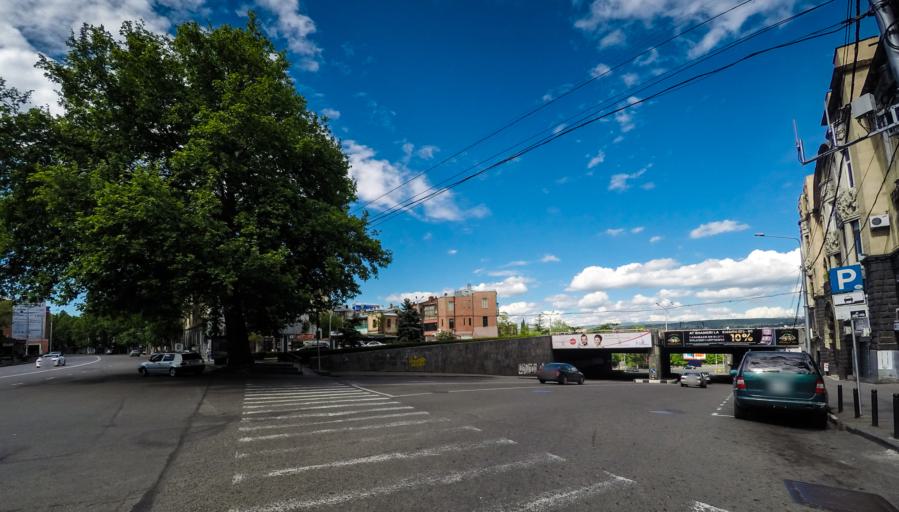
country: GE
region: T'bilisi
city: Tbilisi
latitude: 41.7039
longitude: 44.7905
